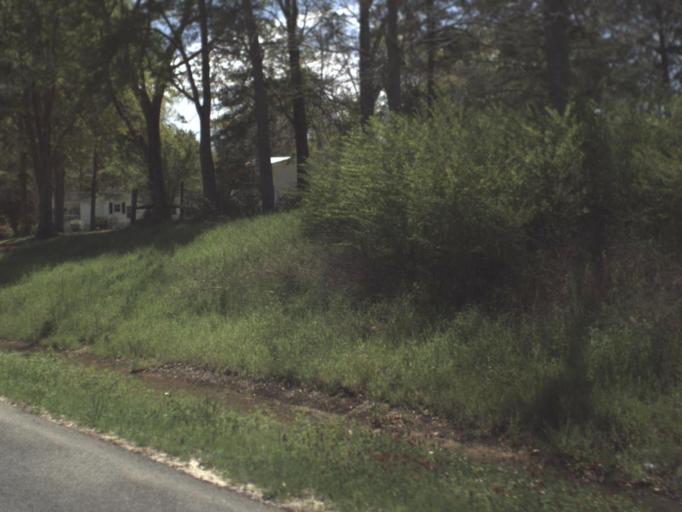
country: US
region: Alabama
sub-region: Geneva County
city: Geneva
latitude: 30.9360
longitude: -85.9680
